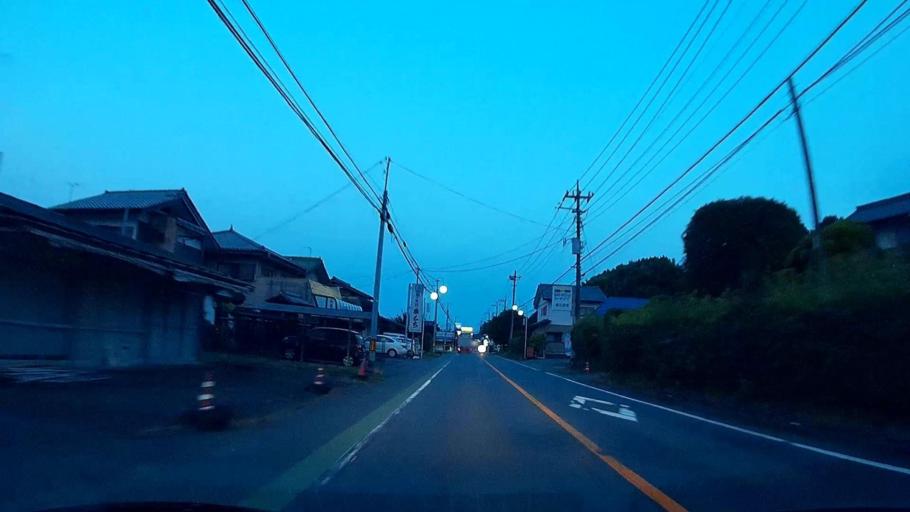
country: JP
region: Gunma
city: Annaka
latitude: 36.3669
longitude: 138.9094
